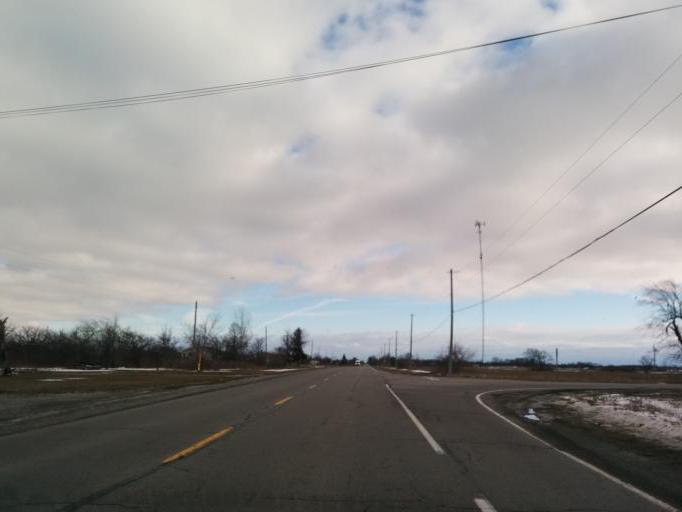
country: CA
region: Ontario
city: Brantford
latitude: 42.9718
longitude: -80.0783
